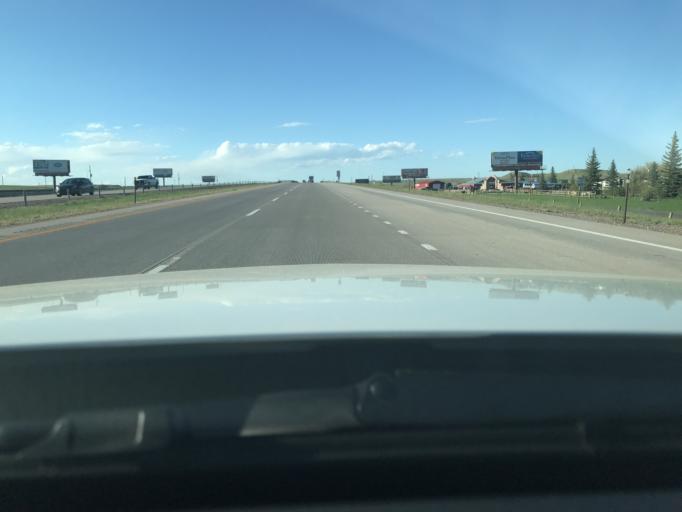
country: US
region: Wyoming
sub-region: Laramie County
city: South Greeley
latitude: 41.0009
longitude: -104.9062
